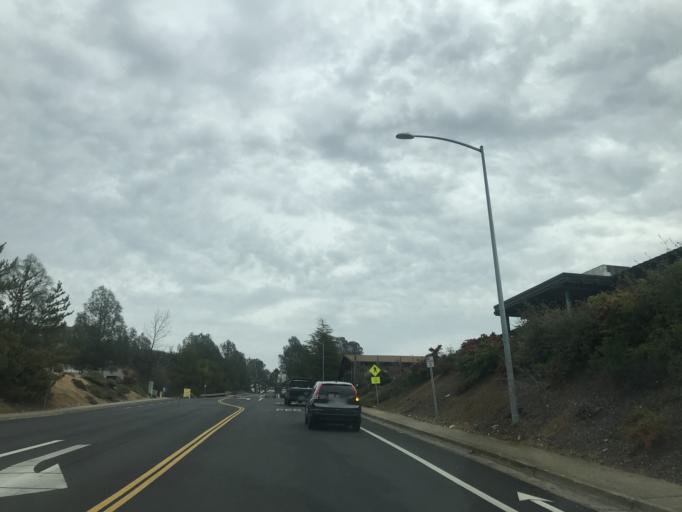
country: US
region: California
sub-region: El Dorado County
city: Placerville
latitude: 38.7284
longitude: -120.8370
